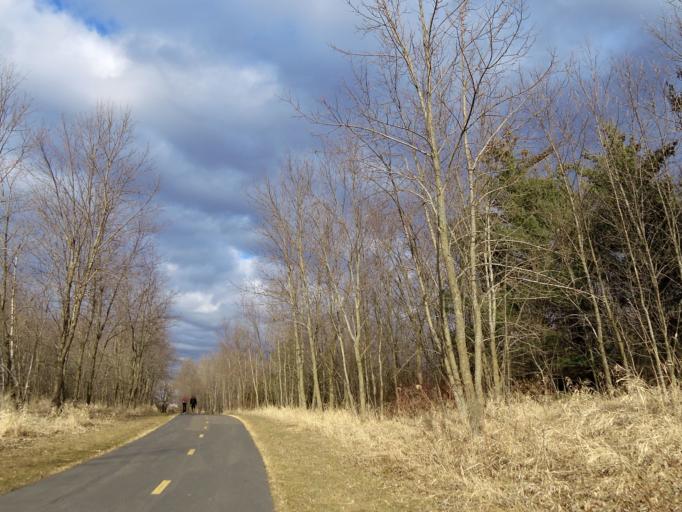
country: US
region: Minnesota
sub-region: Scott County
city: Prior Lake
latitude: 44.6929
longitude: -93.3807
